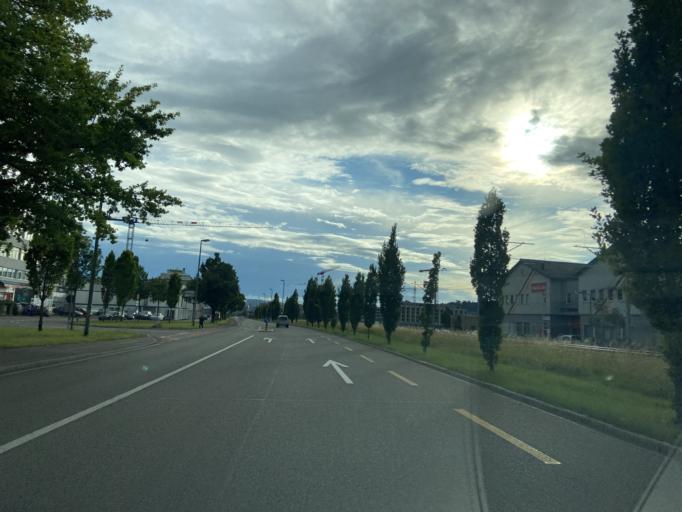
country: CH
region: Zurich
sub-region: Bezirk Winterthur
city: Oberwinterthur (Kreis 2) / Hegi
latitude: 47.5025
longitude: 8.7747
